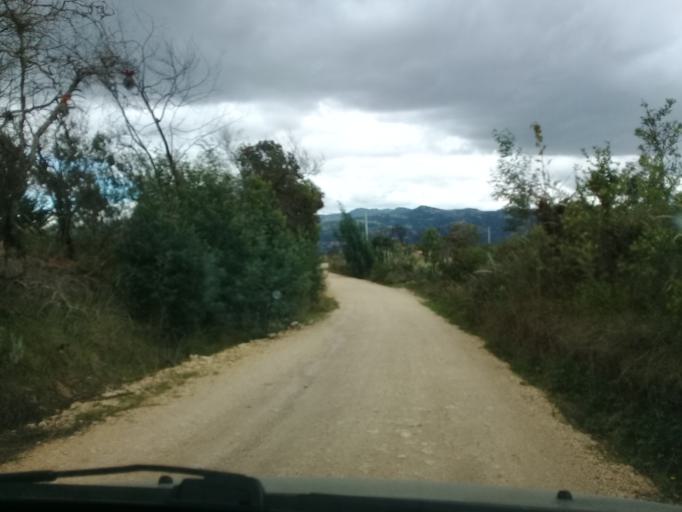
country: CO
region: Cundinamarca
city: Lenguazaque
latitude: 5.2833
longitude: -73.7430
